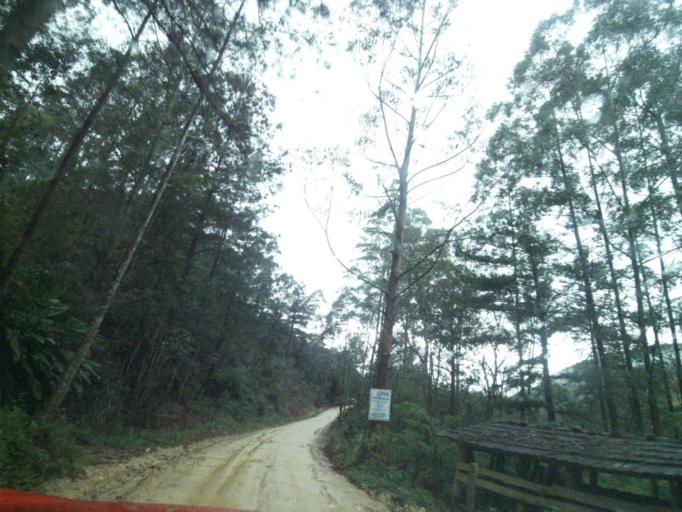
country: BR
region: Santa Catarina
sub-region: Anitapolis
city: Anitapolis
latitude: -27.9171
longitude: -49.1923
